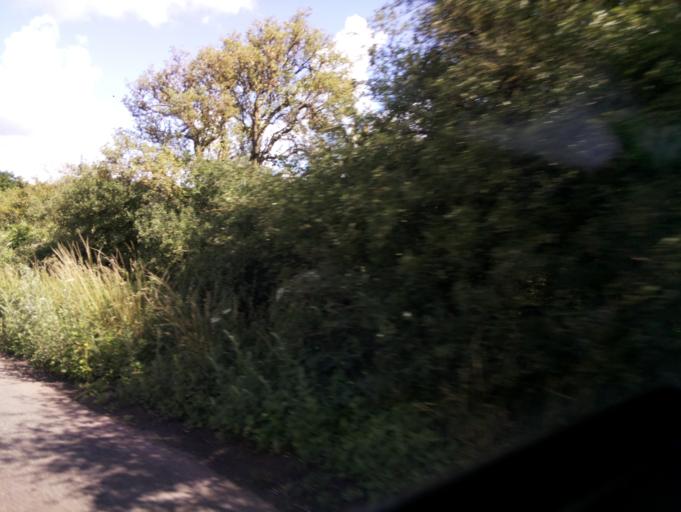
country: GB
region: England
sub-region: Gloucestershire
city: Newent
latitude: 51.9086
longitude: -2.3386
